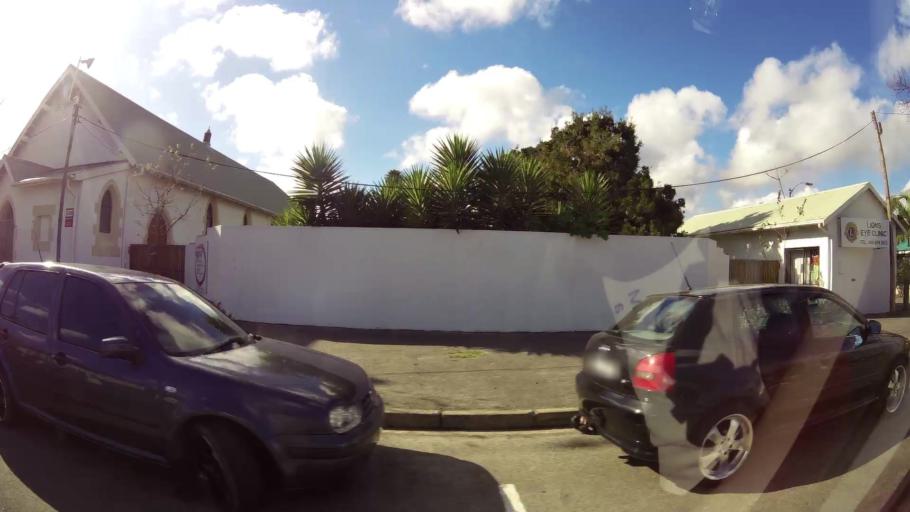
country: ZA
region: Western Cape
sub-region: Eden District Municipality
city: Knysna
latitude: -34.0382
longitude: 23.0508
